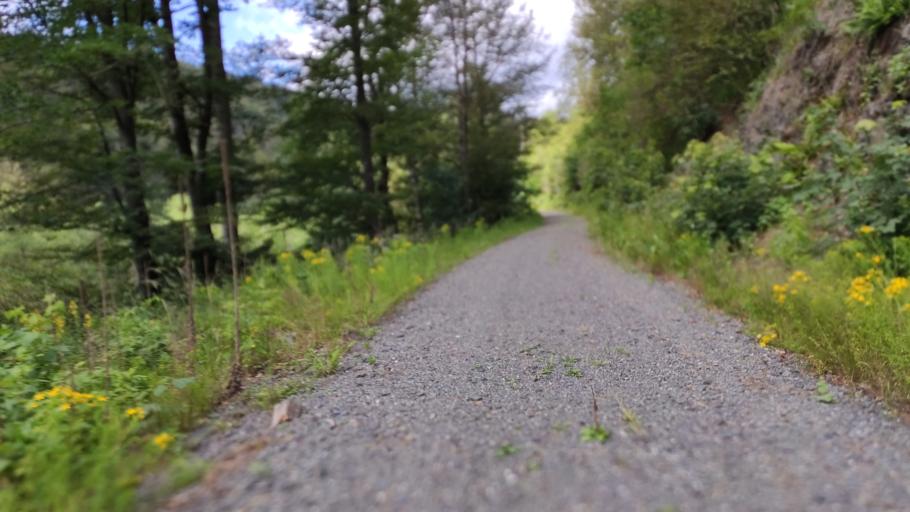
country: DE
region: Bavaria
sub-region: Upper Franconia
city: Nordhalben
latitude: 50.3682
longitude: 11.4821
